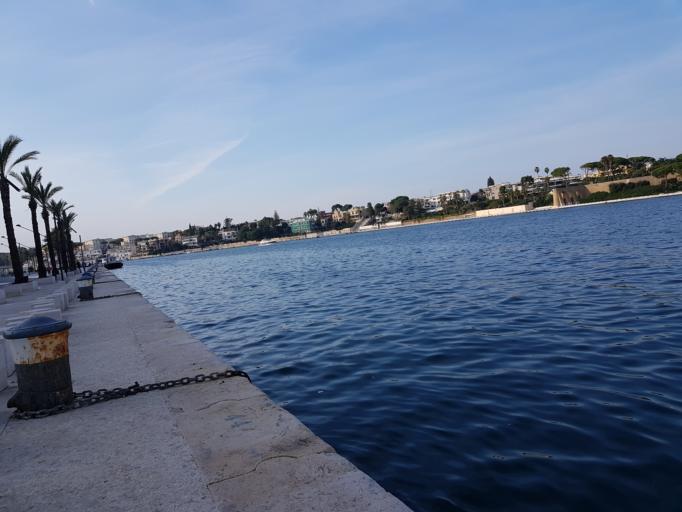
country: IT
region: Apulia
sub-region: Provincia di Brindisi
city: Brindisi
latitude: 40.6414
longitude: 17.9473
